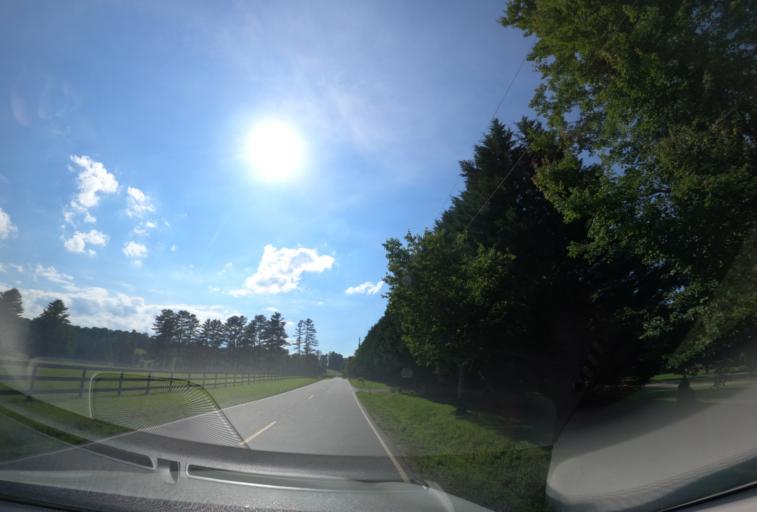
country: US
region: North Carolina
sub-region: Transylvania County
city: Brevard
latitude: 35.2552
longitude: -82.6554
